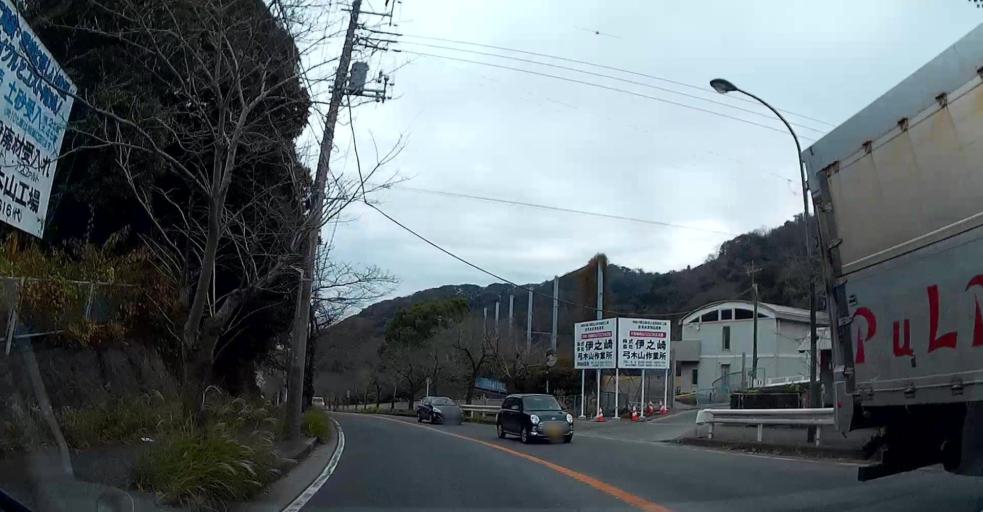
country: JP
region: Kanagawa
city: Yokosuka
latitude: 35.2232
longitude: 139.6640
